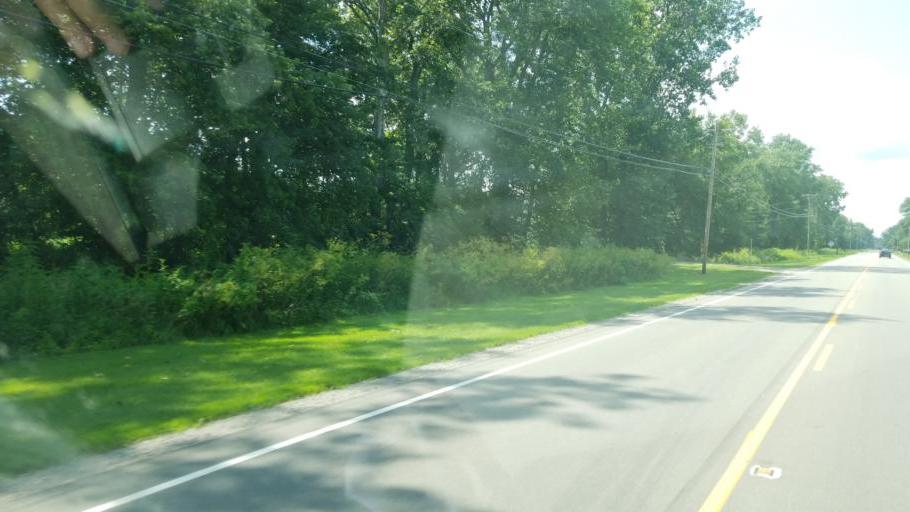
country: US
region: Ohio
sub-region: Coshocton County
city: Coshocton
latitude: 40.3093
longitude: -81.9292
